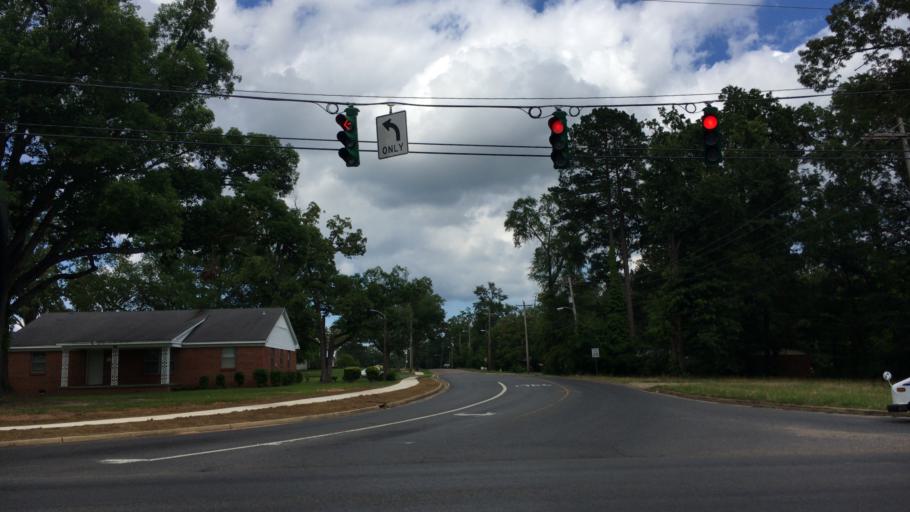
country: US
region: Louisiana
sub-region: Lincoln Parish
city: Ruston
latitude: 32.5151
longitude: -92.6386
